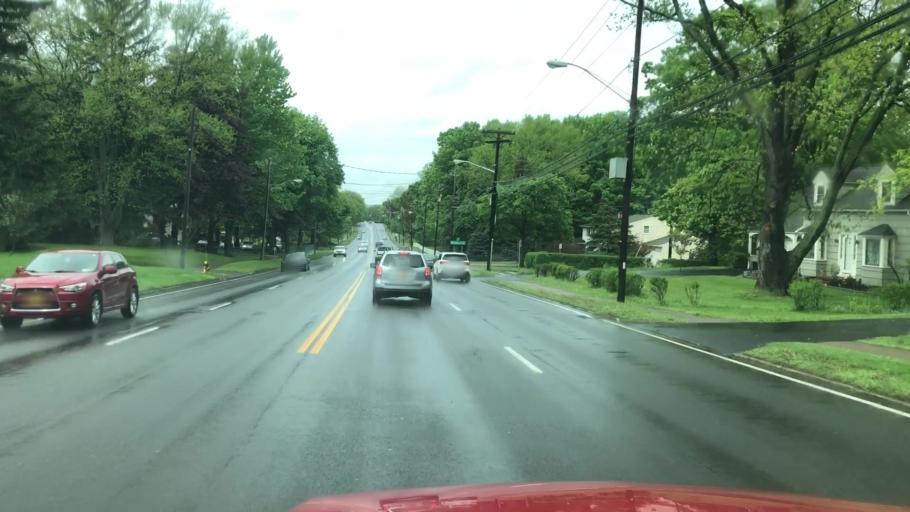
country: US
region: New York
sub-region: Monroe County
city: Fairport
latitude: 43.1311
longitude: -77.4565
